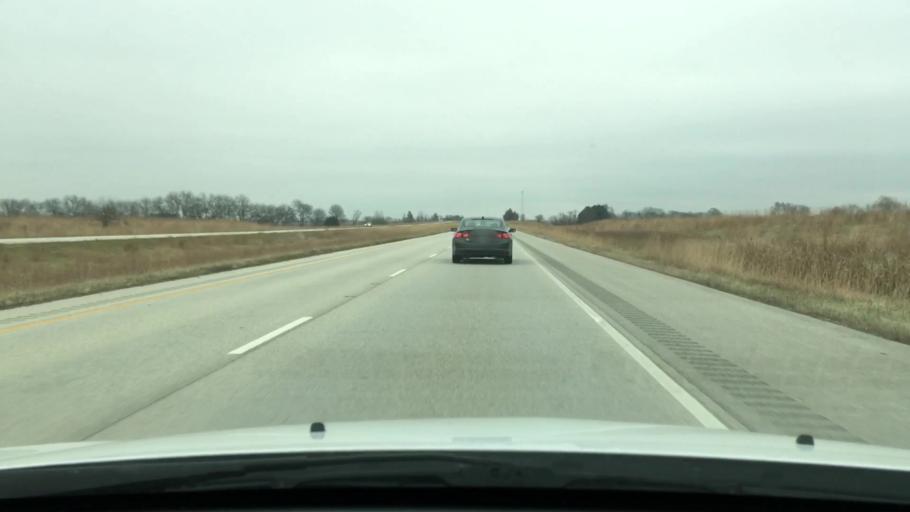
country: US
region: Illinois
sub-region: Sangamon County
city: New Berlin
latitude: 39.7403
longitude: -89.8918
